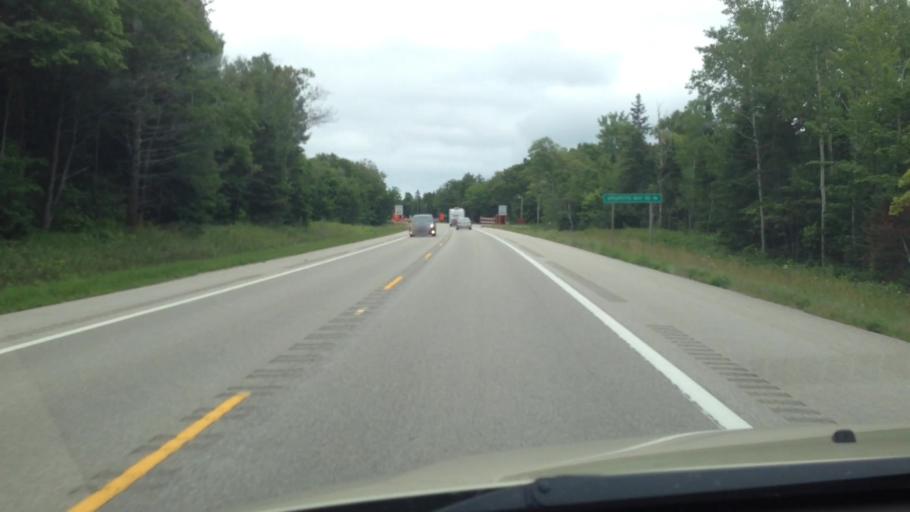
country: US
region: Michigan
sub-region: Luce County
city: Newberry
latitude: 46.0566
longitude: -85.1611
